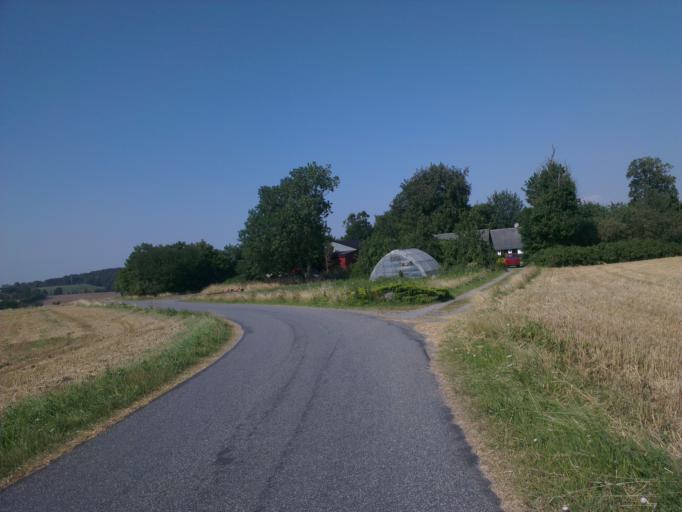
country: DK
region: Capital Region
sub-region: Frederikssund Kommune
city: Skibby
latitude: 55.7515
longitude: 11.9495
